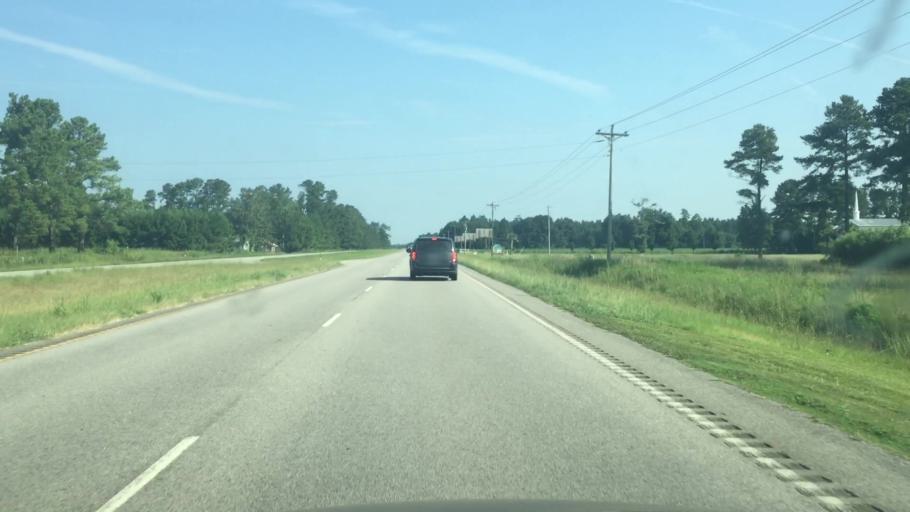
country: US
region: South Carolina
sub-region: Horry County
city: Little River
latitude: 33.9676
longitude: -78.7398
